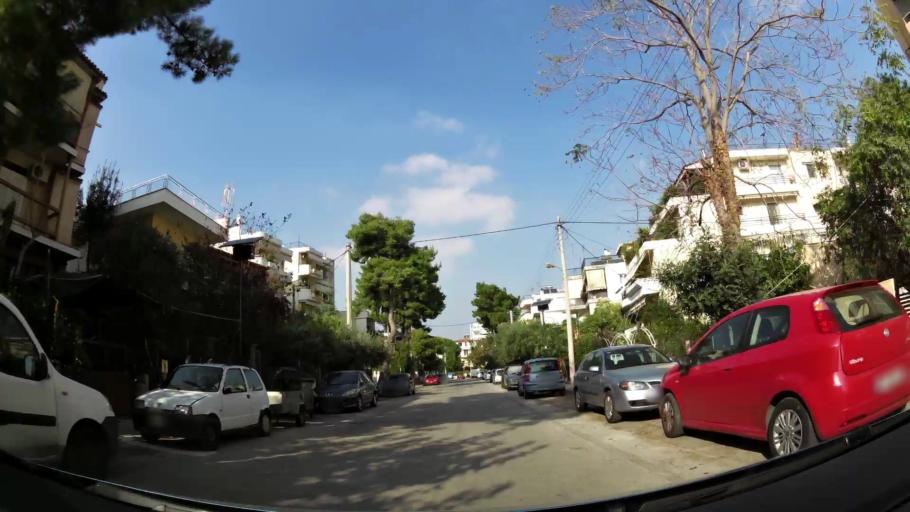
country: GR
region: Attica
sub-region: Nomarchia Athinas
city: Cholargos
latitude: 37.9998
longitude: 23.8110
